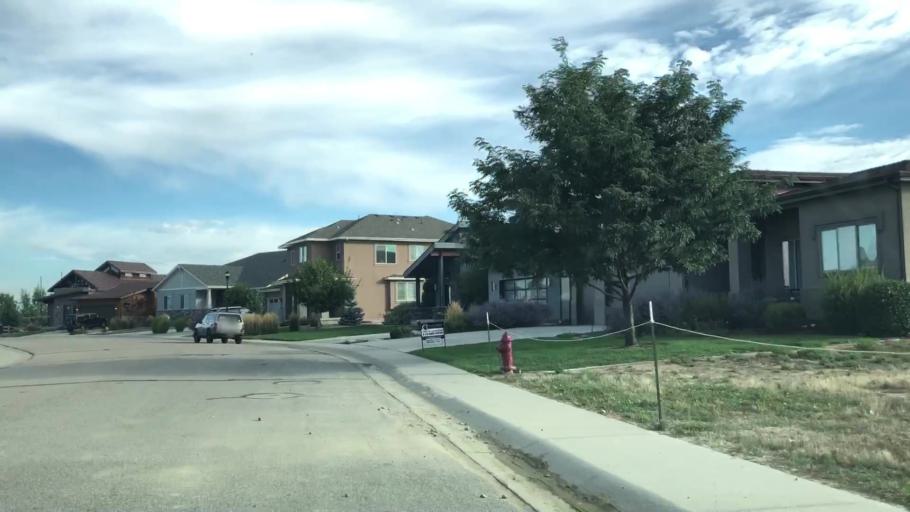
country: US
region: Colorado
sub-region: Weld County
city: Windsor
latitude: 40.4490
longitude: -104.9760
